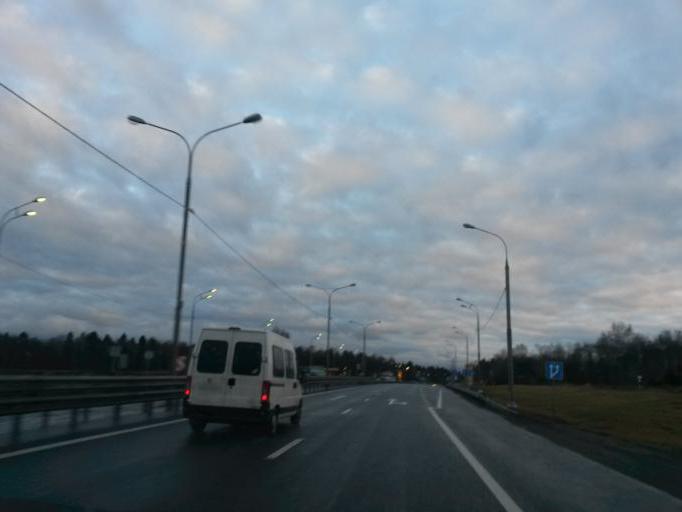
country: RU
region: Moskovskaya
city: Svatkovo
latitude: 56.3407
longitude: 38.2635
